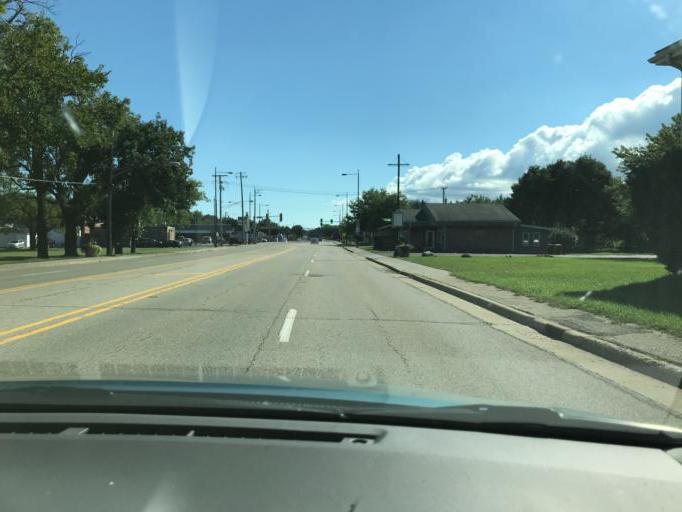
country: US
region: Illinois
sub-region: Lake County
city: Winthrop Harbor
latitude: 42.4839
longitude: -87.8226
